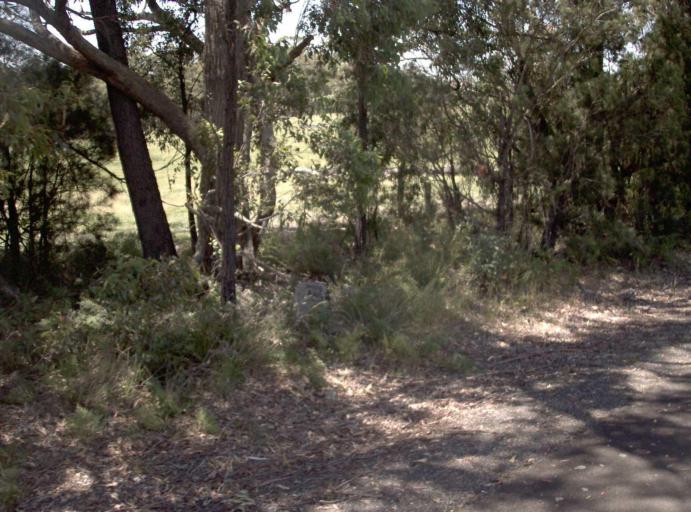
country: AU
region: Victoria
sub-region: East Gippsland
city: Lakes Entrance
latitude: -37.7351
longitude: 148.1467
